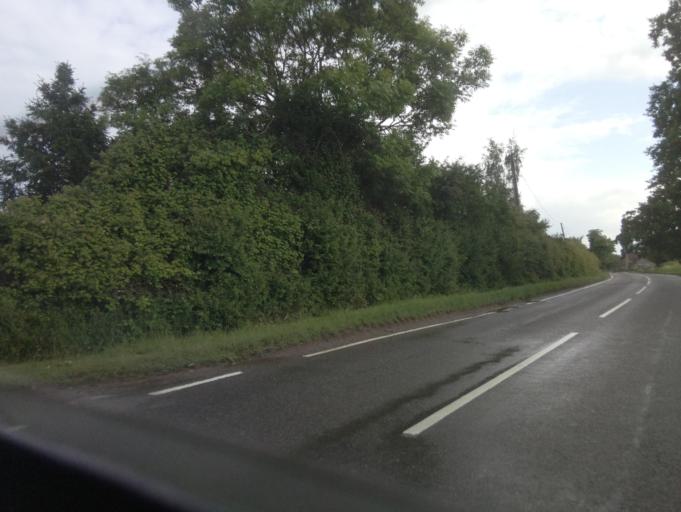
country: GB
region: England
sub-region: Lincolnshire
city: Great Gonerby
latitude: 53.0349
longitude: -0.6511
